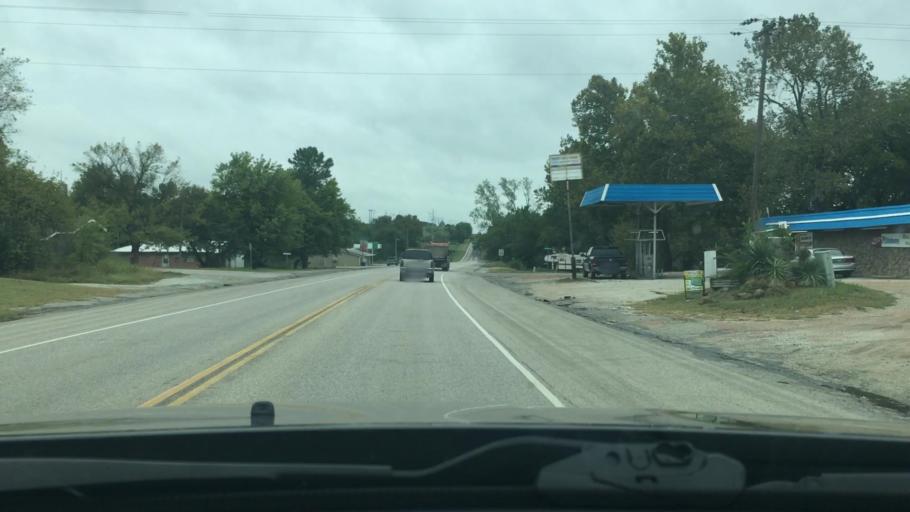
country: US
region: Oklahoma
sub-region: Pontotoc County
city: Ada
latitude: 34.6137
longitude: -96.6347
